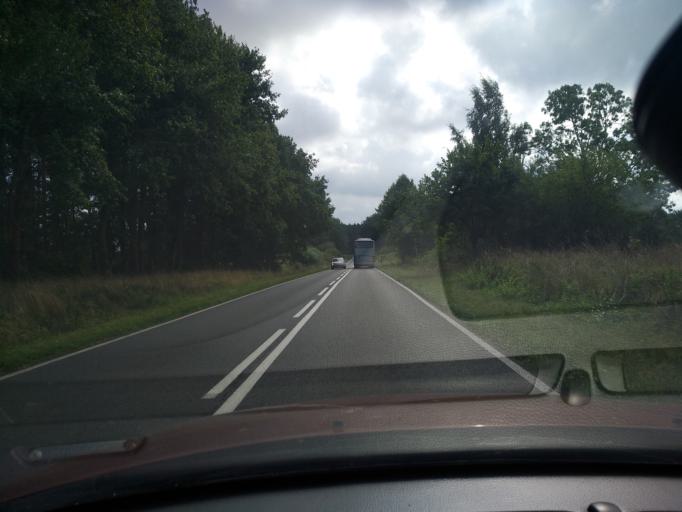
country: PL
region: West Pomeranian Voivodeship
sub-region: Powiat kamienski
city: Wolin
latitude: 53.9792
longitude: 14.6293
